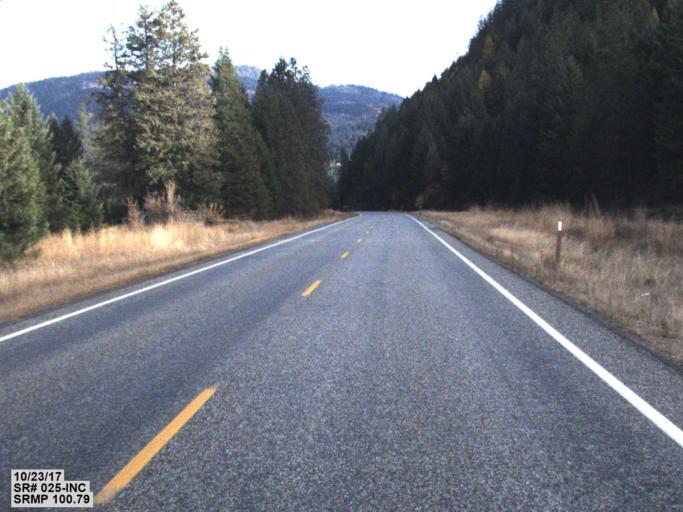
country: US
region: Washington
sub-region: Stevens County
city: Kettle Falls
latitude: 48.8145
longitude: -117.9682
